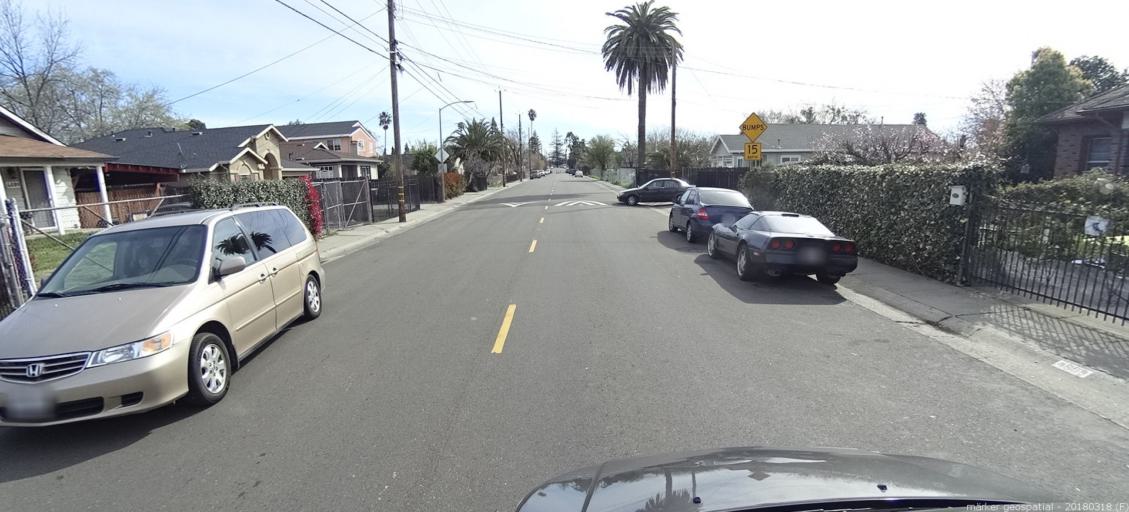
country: US
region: California
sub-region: Sacramento County
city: Parkway
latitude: 38.5352
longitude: -121.4528
